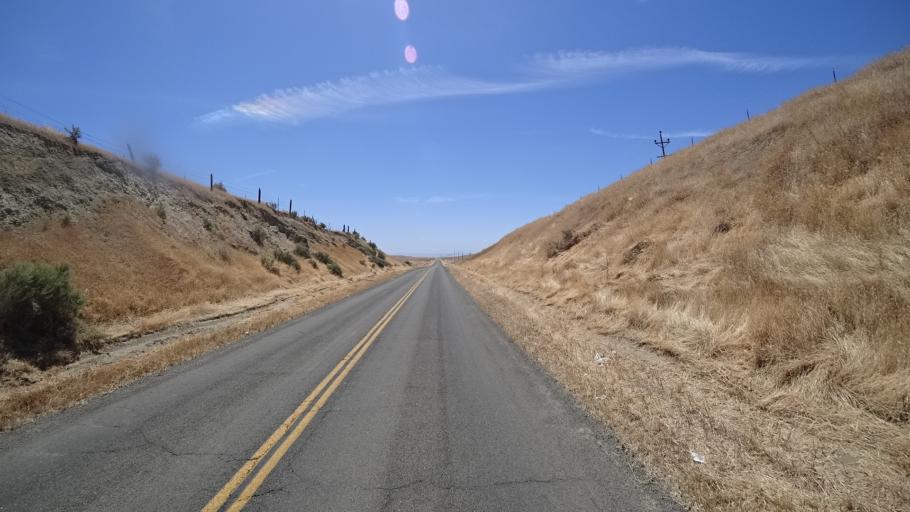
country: US
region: California
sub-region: Kings County
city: Kettleman City
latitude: 35.8904
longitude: -119.9151
